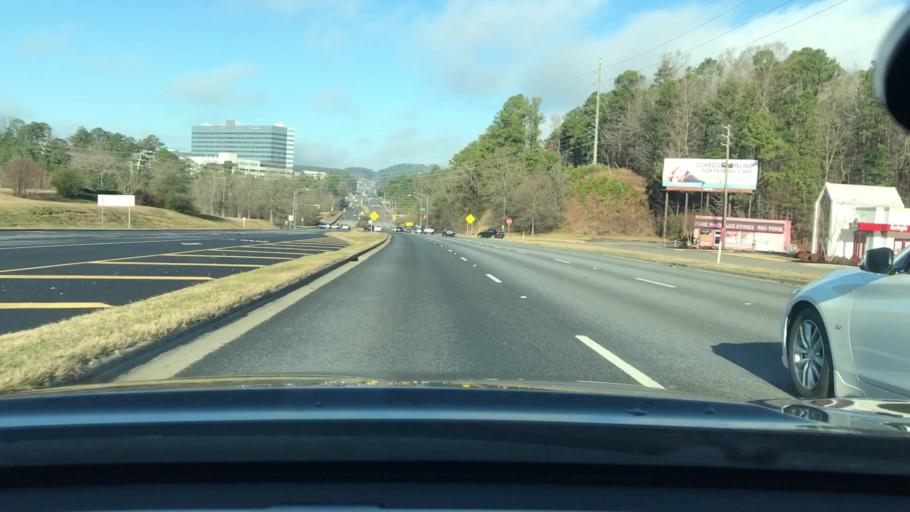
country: US
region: Alabama
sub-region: Shelby County
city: Lake Purdy
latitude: 33.4294
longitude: -86.7090
